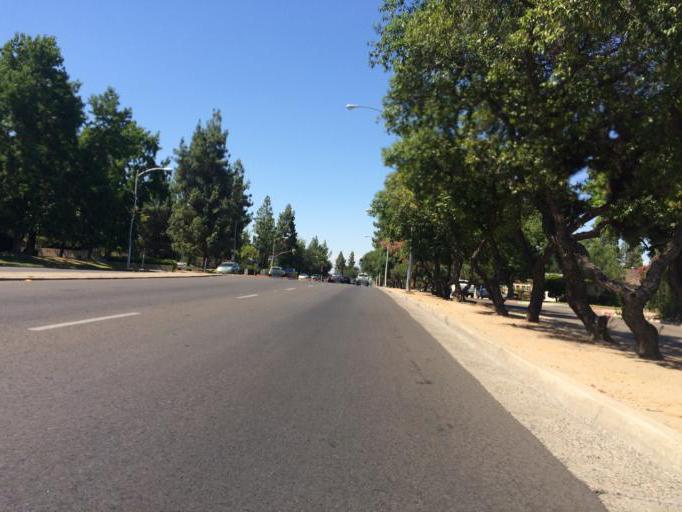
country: US
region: California
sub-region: Fresno County
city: Fresno
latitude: 36.8037
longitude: -119.7722
